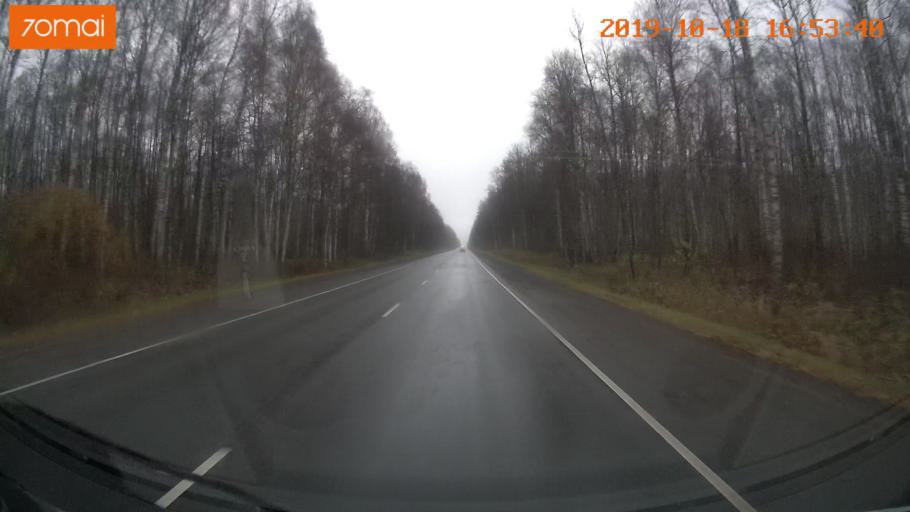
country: RU
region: Ivanovo
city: Nerl'
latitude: 56.6181
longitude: 40.5623
